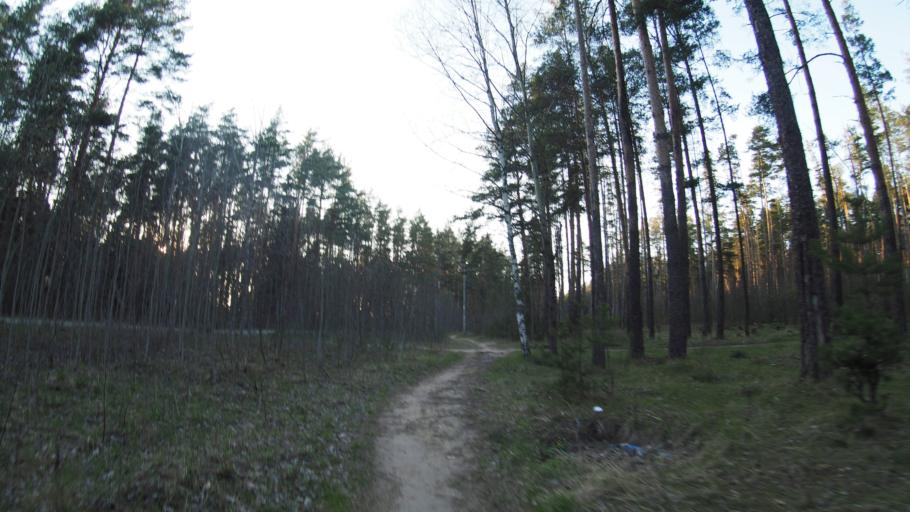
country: RU
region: Moskovskaya
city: Malyshevo
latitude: 55.5143
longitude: 38.3310
